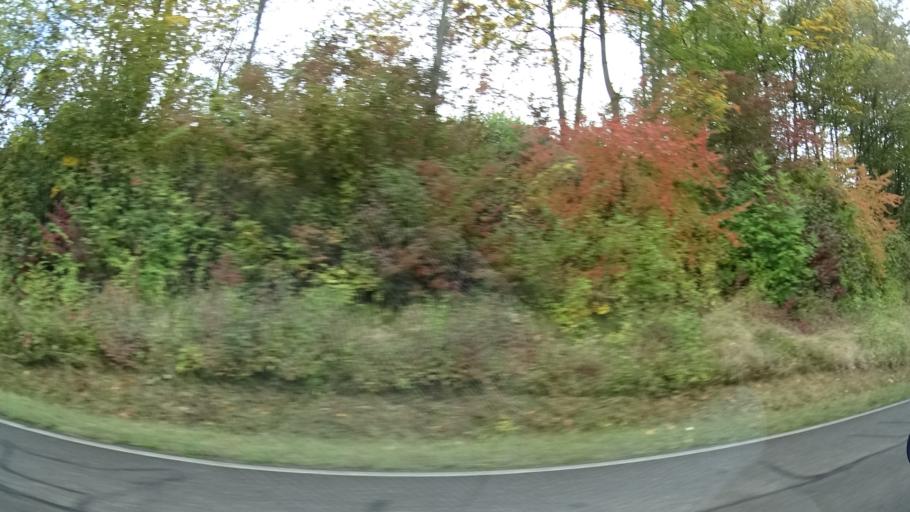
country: DE
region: Baden-Wuerttemberg
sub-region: Karlsruhe Region
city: Ostringen
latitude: 49.1972
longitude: 8.6890
